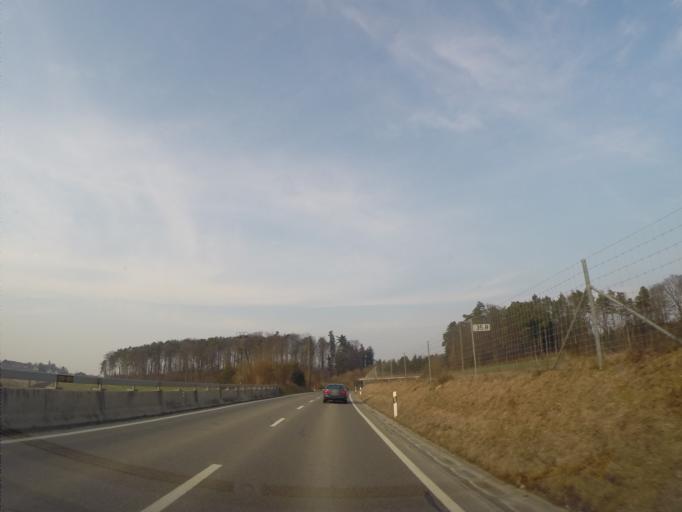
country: CH
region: Zurich
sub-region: Bezirk Andelfingen
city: Henggart
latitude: 47.5540
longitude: 8.6871
